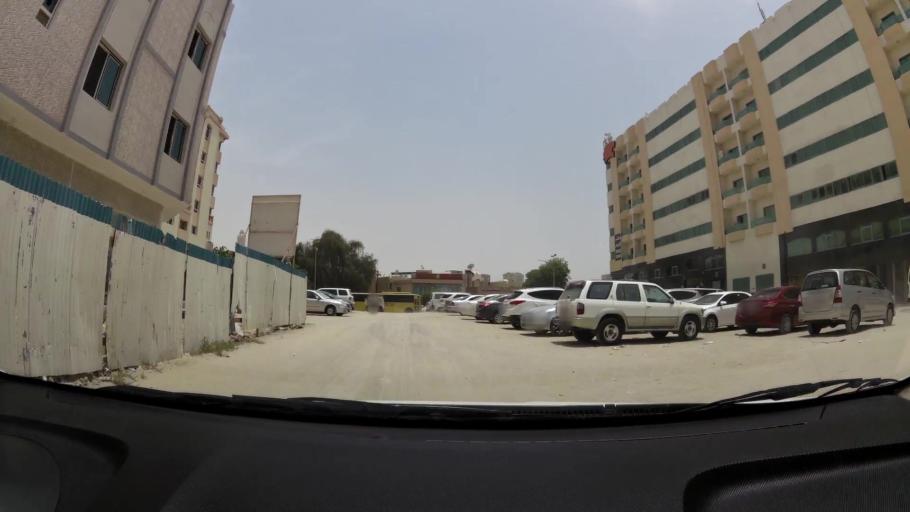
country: AE
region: Ash Shariqah
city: Sharjah
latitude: 25.3549
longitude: 55.3964
